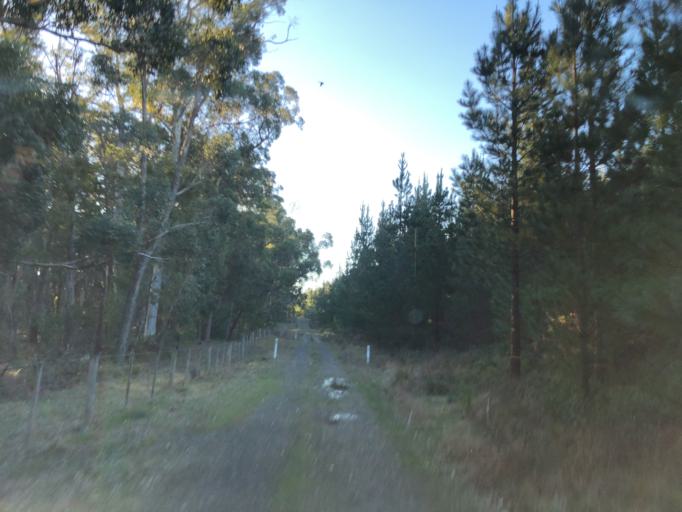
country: AU
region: Victoria
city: Brown Hill
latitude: -37.4975
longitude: 144.1450
